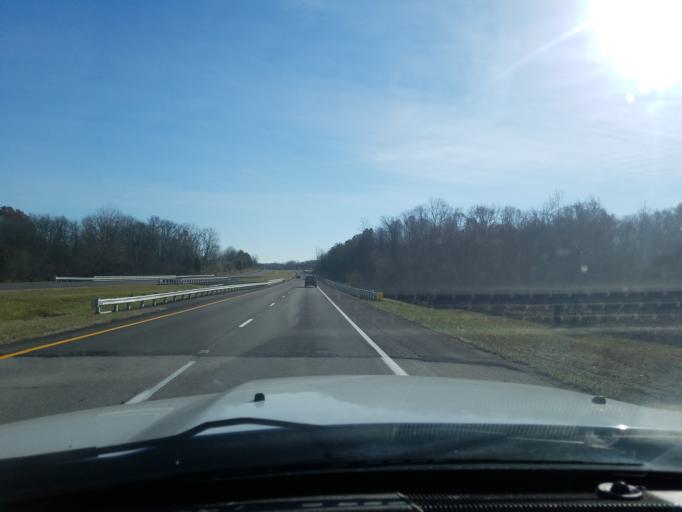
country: US
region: Ohio
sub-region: Brown County
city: Mount Orab
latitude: 39.0231
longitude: -83.8713
